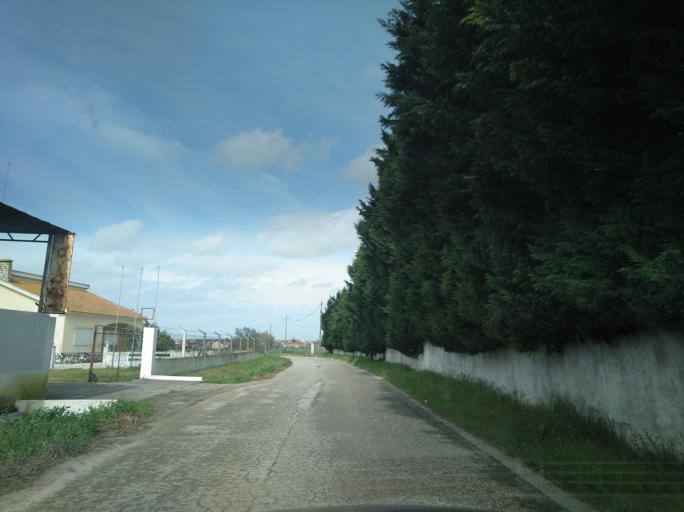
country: PT
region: Setubal
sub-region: Palmela
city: Pinhal Novo
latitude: 38.6679
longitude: -8.9196
